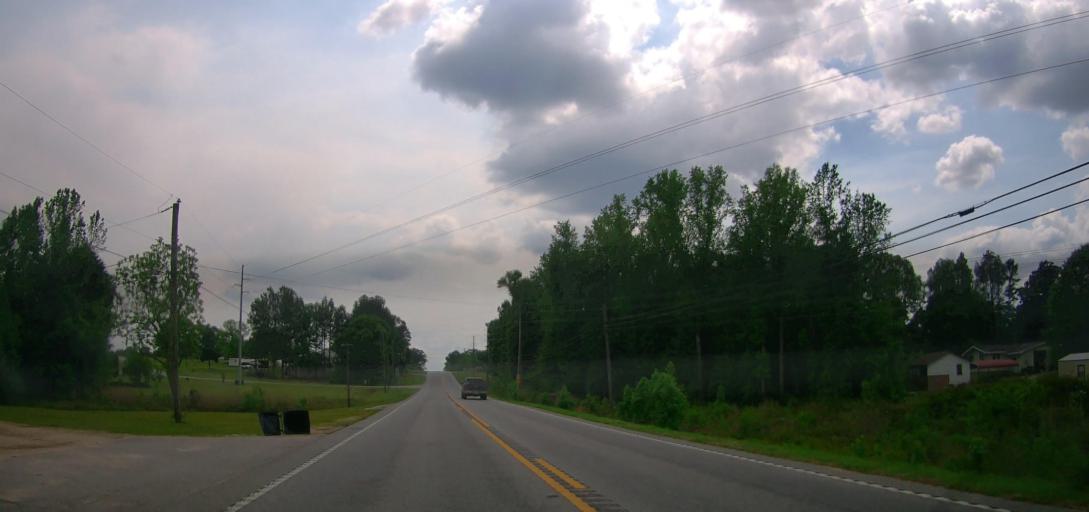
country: US
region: Georgia
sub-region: Treutlen County
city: Soperton
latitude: 32.3677
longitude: -82.5955
